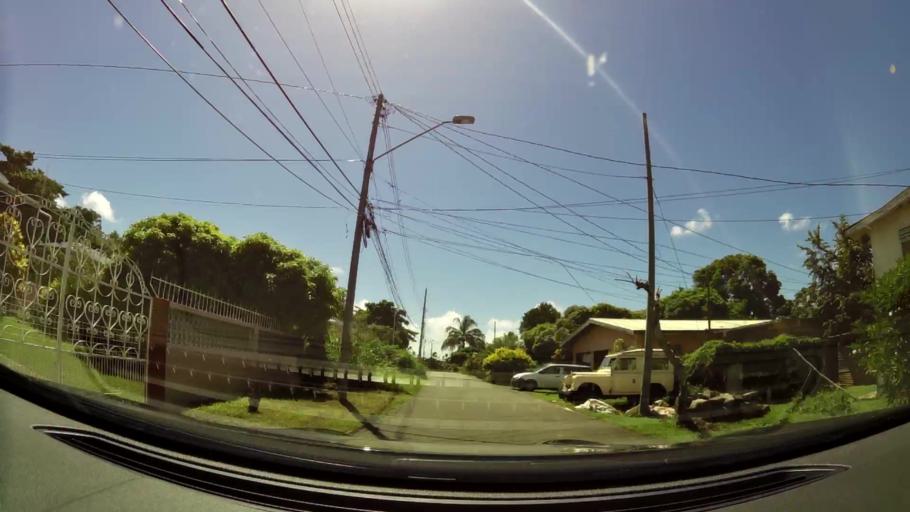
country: TT
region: Tobago
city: Scarborough
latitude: 11.1717
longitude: -60.8007
